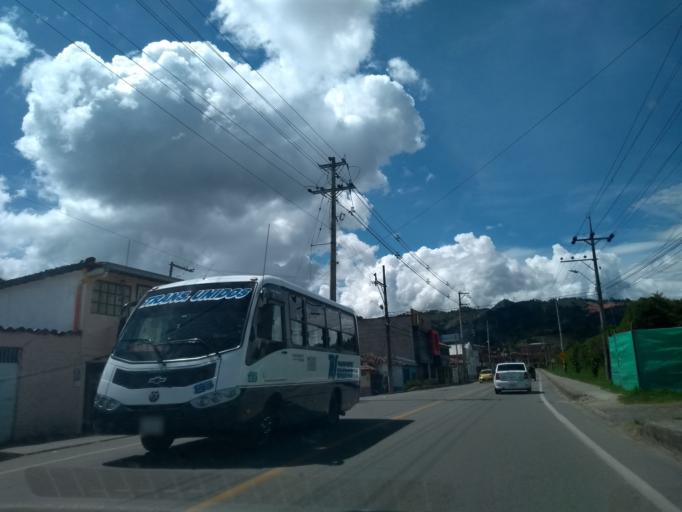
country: CO
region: Antioquia
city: La Ceja
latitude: 6.0356
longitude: -75.4244
